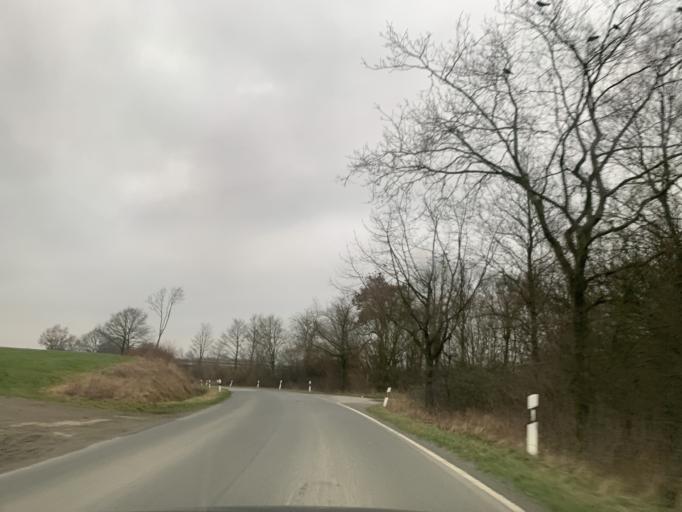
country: DE
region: Schleswig-Holstein
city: Meddewade
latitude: 53.7987
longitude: 10.4458
